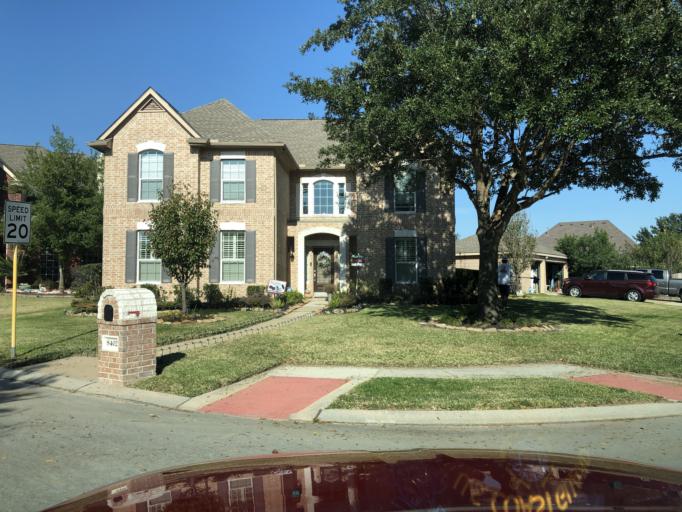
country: US
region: Texas
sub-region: Harris County
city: Tomball
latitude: 30.0344
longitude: -95.5488
